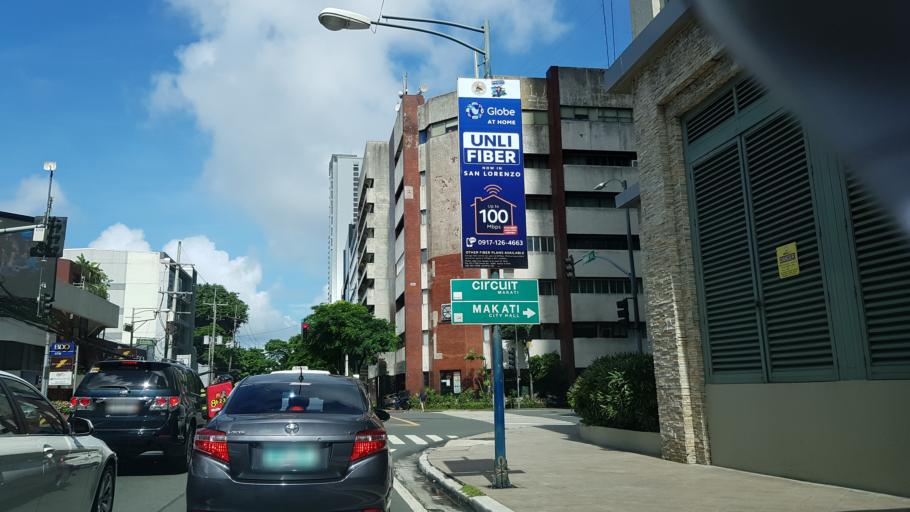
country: PH
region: Metro Manila
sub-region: Makati City
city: Makati City
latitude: 14.5508
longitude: 121.0198
